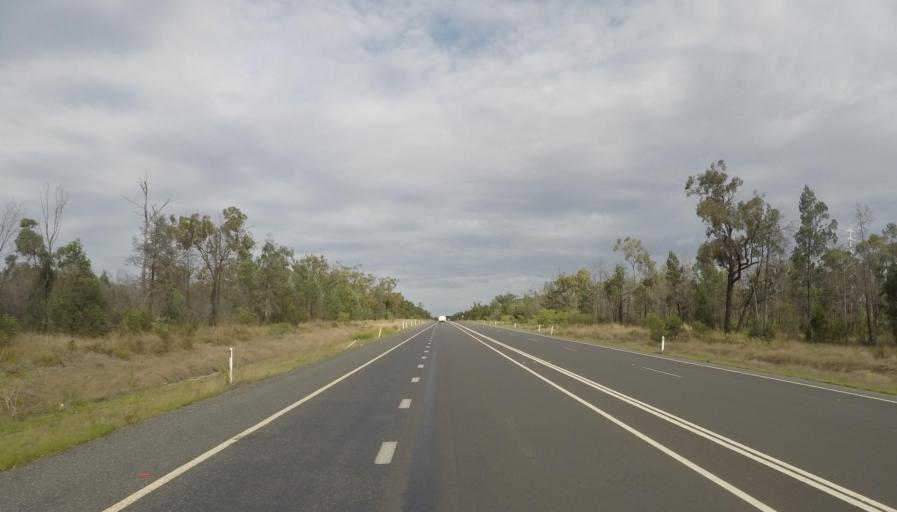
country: AU
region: Queensland
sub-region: Western Downs
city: Westcourt
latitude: -26.6680
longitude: 150.3125
